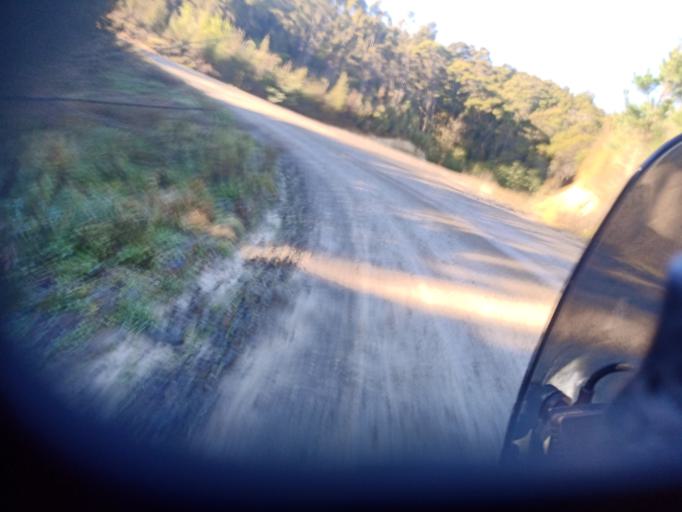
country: NZ
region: Gisborne
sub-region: Gisborne District
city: Gisborne
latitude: -38.1823
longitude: 178.1197
